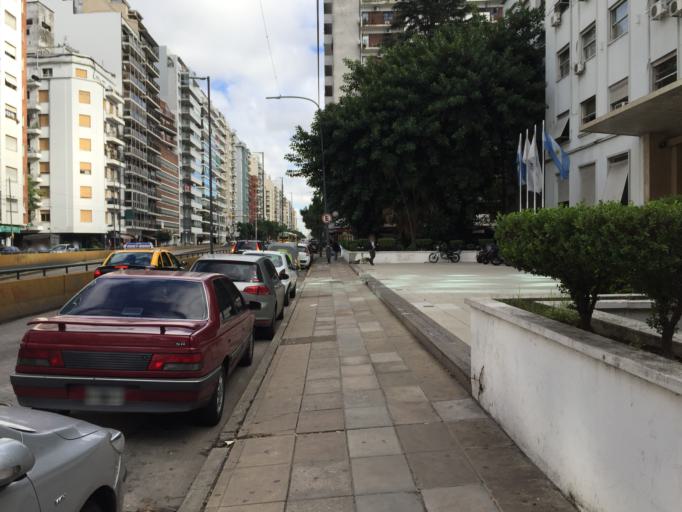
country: AR
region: Buenos Aires F.D.
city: Colegiales
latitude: -34.5745
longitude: -58.4366
